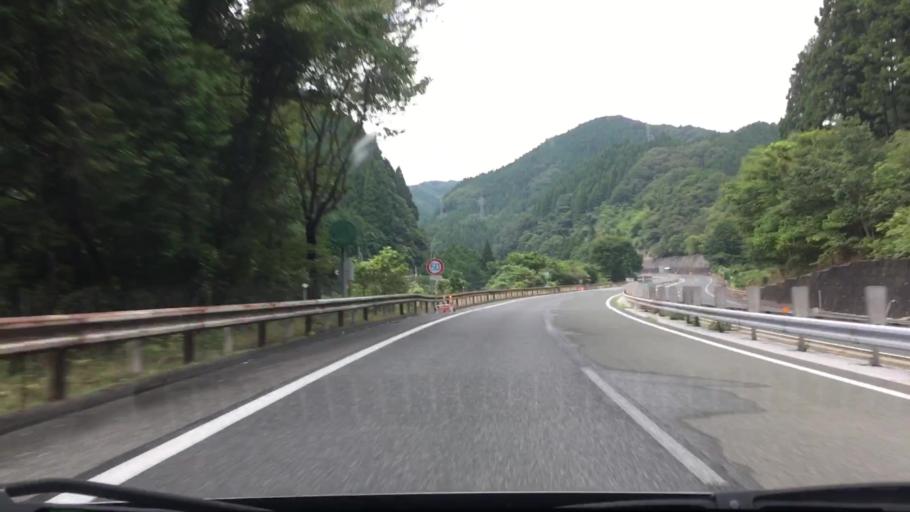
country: JP
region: Okayama
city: Niimi
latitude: 35.0164
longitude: 133.4289
